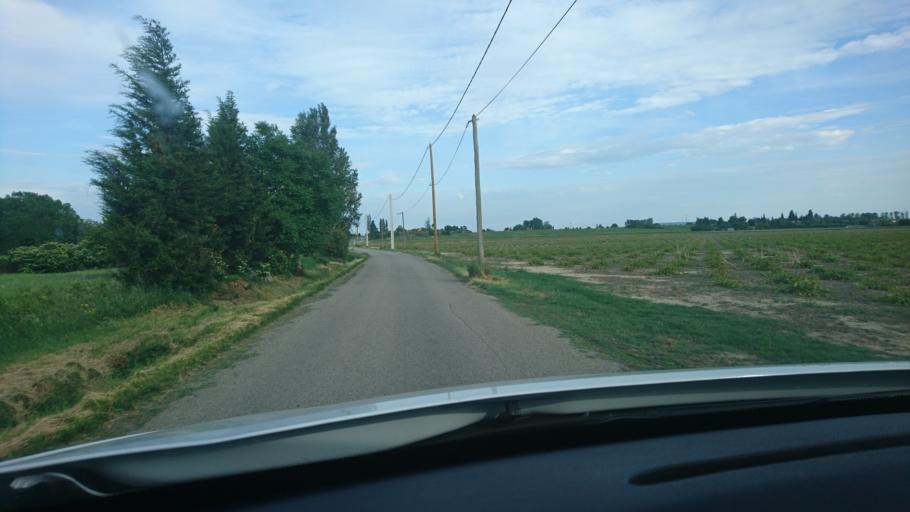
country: FR
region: Provence-Alpes-Cote d'Azur
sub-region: Departement du Vaucluse
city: Jonquieres
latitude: 44.1332
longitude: 4.8835
